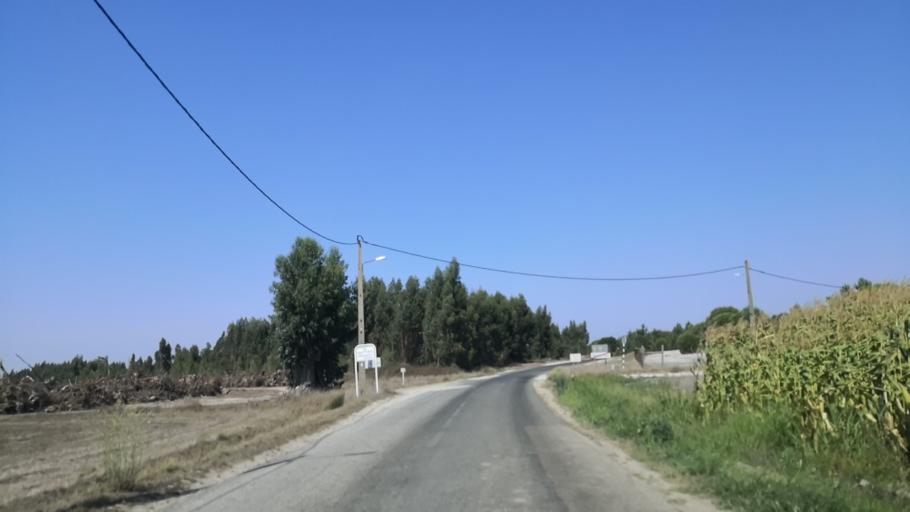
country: PT
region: Santarem
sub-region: Benavente
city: Poceirao
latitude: 38.7213
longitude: -8.7094
